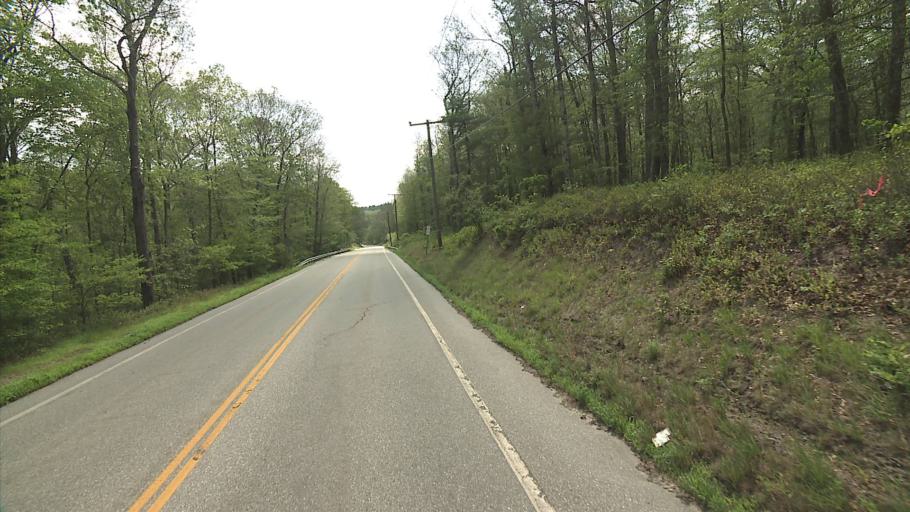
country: US
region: Rhode Island
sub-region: Washington County
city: Hope Valley
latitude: 41.5727
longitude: -71.7957
